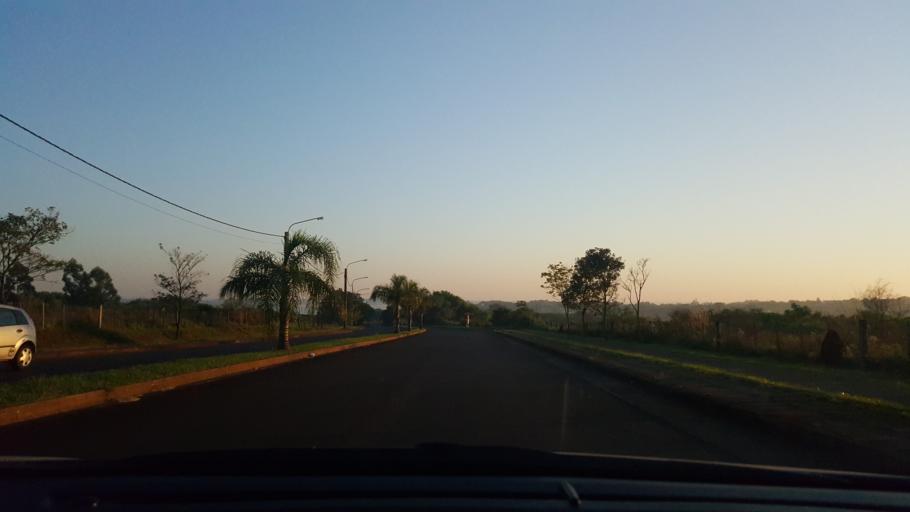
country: AR
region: Misiones
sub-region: Departamento de Capital
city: Posadas
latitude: -27.3781
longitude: -55.9618
